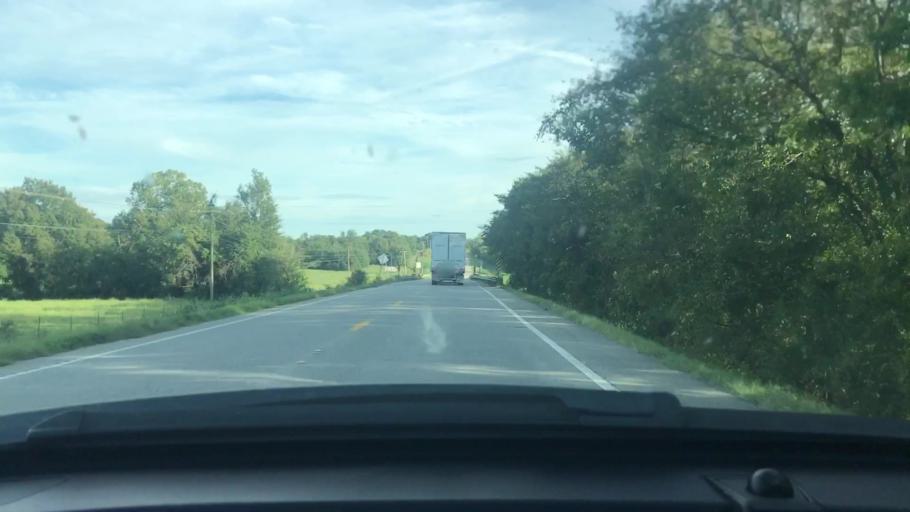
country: US
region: Arkansas
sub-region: Randolph County
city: Pocahontas
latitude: 36.1944
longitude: -91.1668
